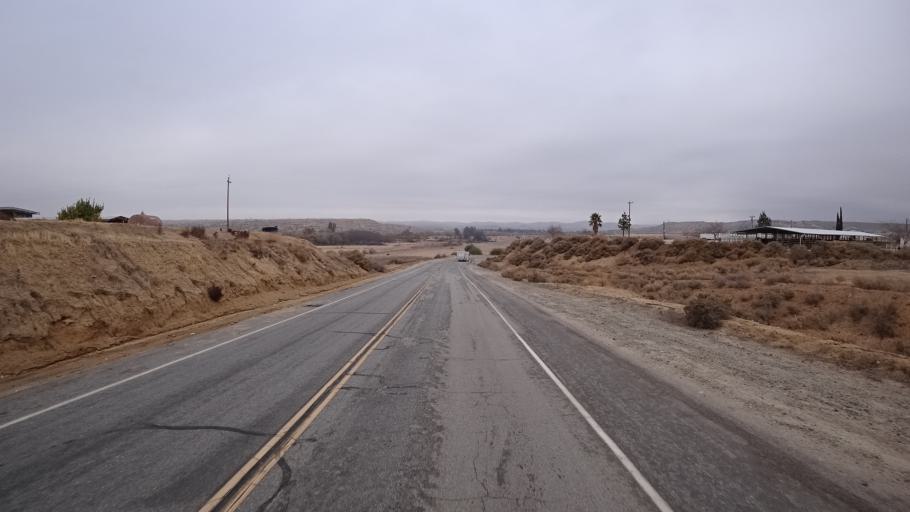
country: US
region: California
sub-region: Kern County
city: Oildale
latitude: 35.4190
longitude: -118.9559
